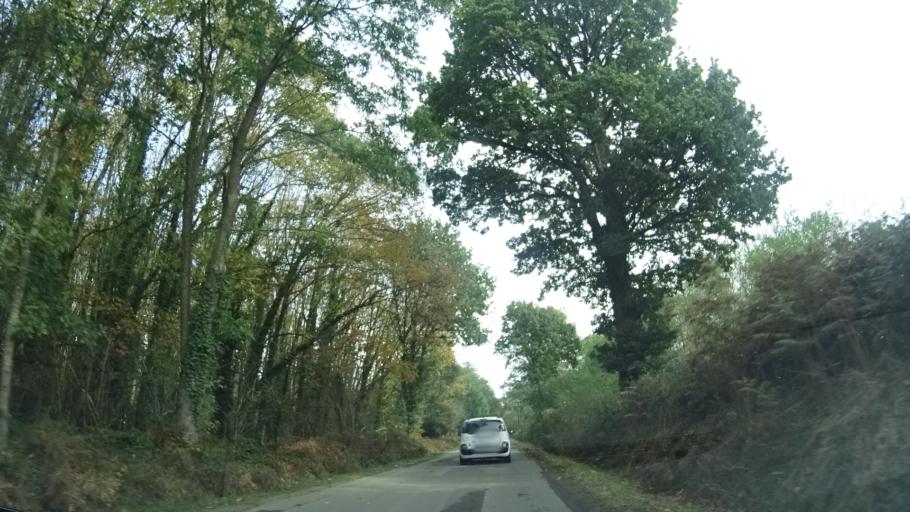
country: FR
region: Brittany
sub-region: Departement d'Ille-et-Vilaine
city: Bonnemain
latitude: 48.4573
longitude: -1.7902
